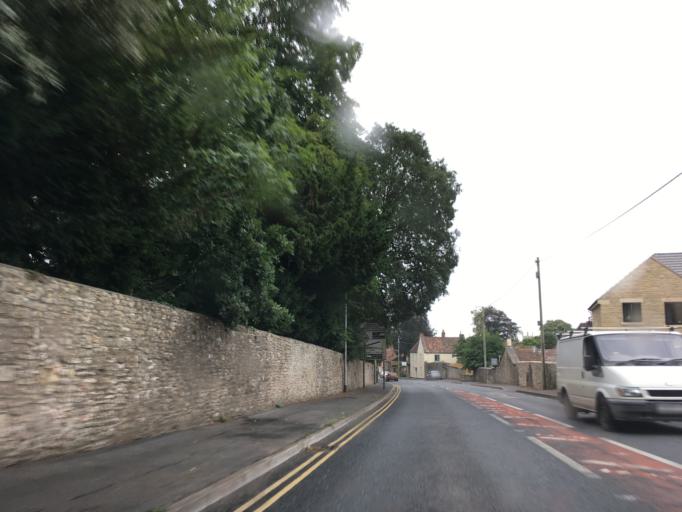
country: GB
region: England
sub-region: Somerset
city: Wells
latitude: 51.2149
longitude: -2.6460
